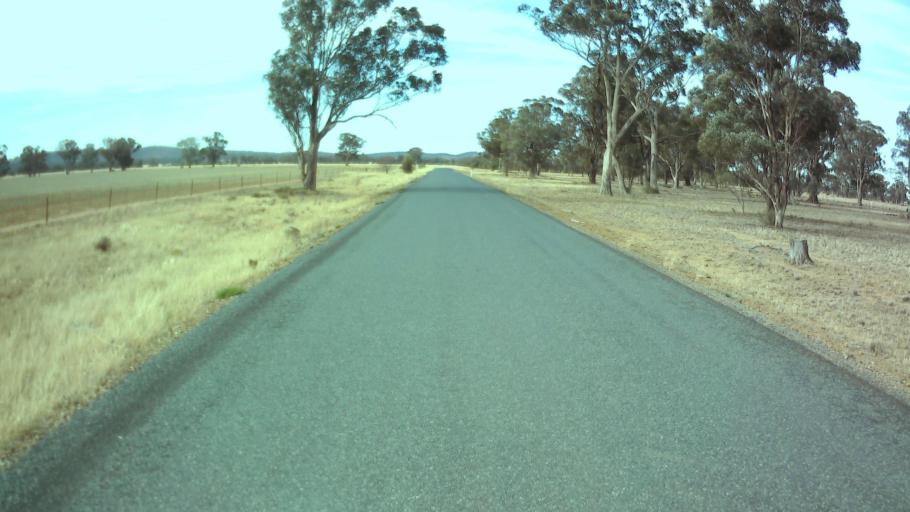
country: AU
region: New South Wales
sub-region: Weddin
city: Grenfell
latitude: -33.8594
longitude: 147.8602
